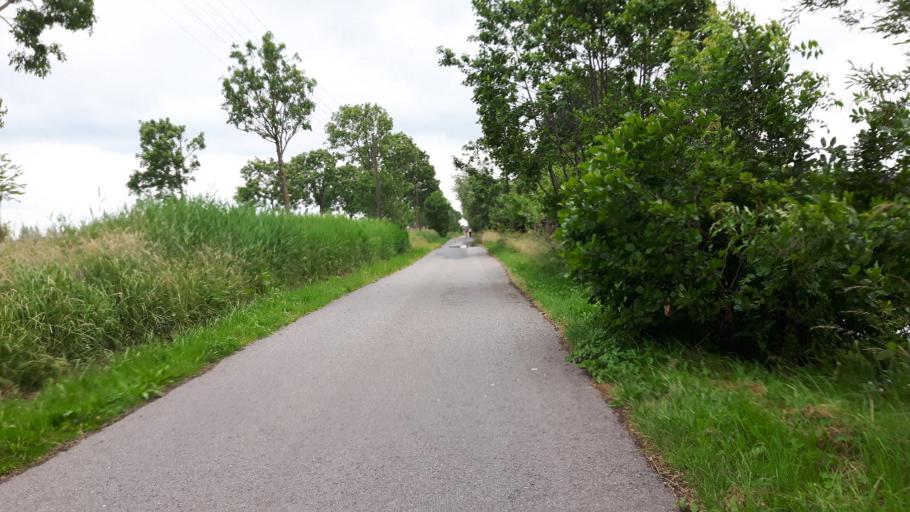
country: NL
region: Utrecht
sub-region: Gemeente Oudewater
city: Oudewater
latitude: 52.0528
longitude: 4.8474
